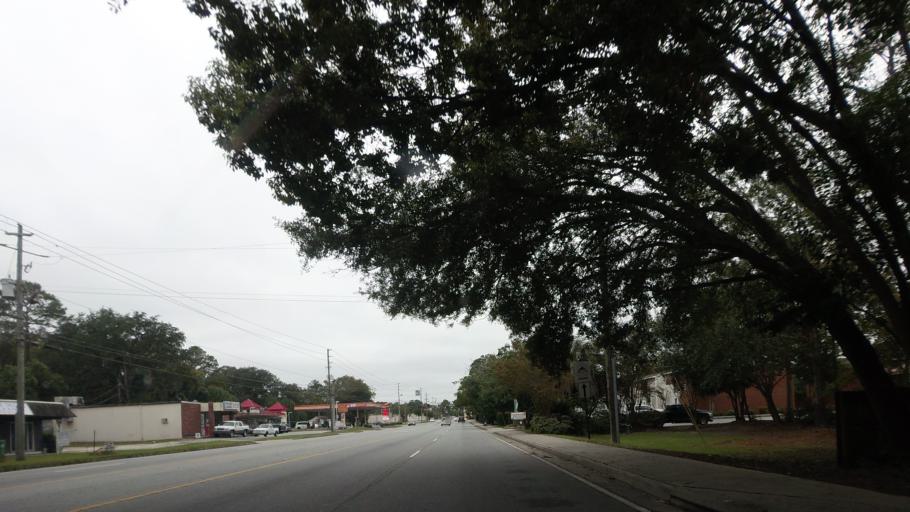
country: US
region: Georgia
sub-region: Lowndes County
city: Valdosta
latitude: 30.8570
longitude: -83.2769
